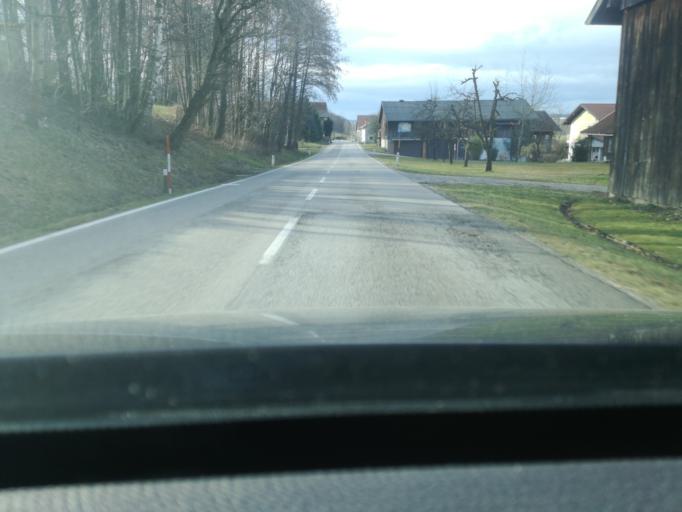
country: AT
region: Upper Austria
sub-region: Politischer Bezirk Ried im Innkreis
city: Waldzell
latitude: 48.1625
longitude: 13.4237
